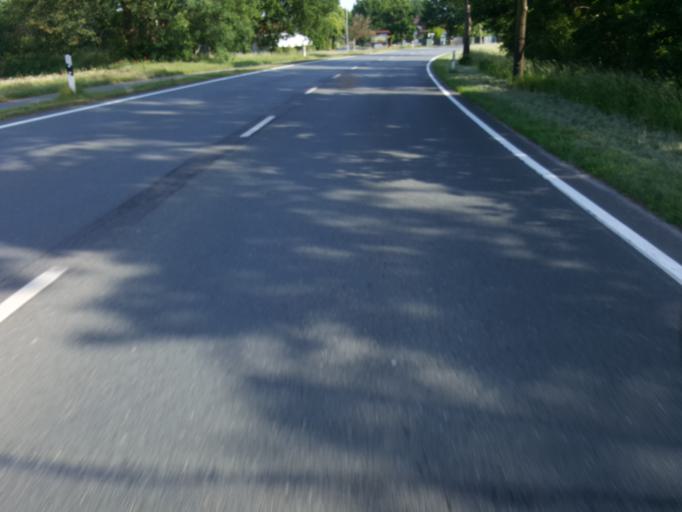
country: DE
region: Lower Saxony
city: Estorf
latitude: 52.5839
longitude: 9.1388
